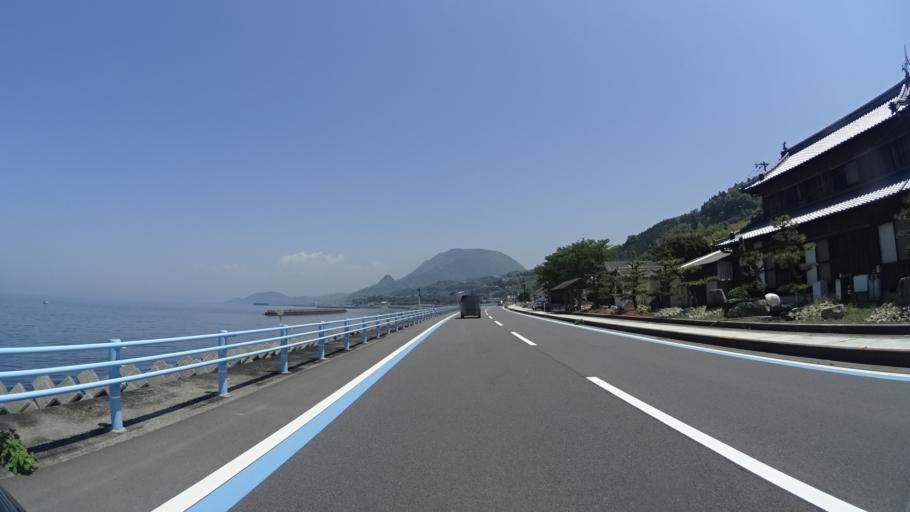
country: JP
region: Ehime
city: Iyo
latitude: 33.6779
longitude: 132.6201
